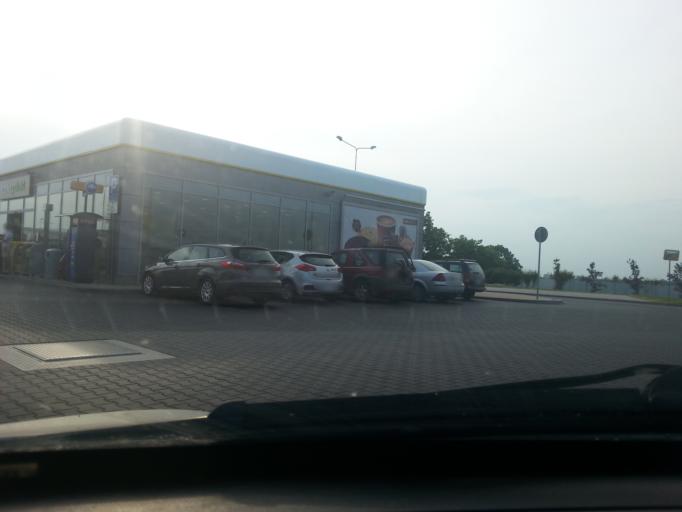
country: PL
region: Masovian Voivodeship
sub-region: Powiat pruszkowski
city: Brwinow
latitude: 52.1560
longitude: 20.6877
